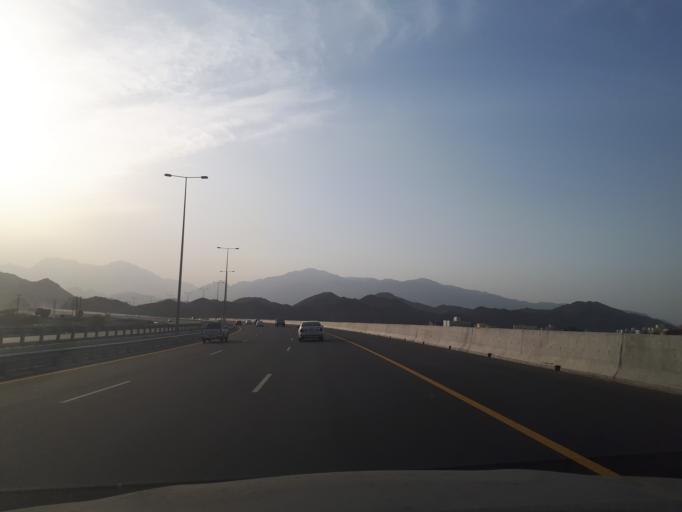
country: OM
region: Muhafazat ad Dakhiliyah
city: Bidbid
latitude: 23.3412
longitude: 58.1079
